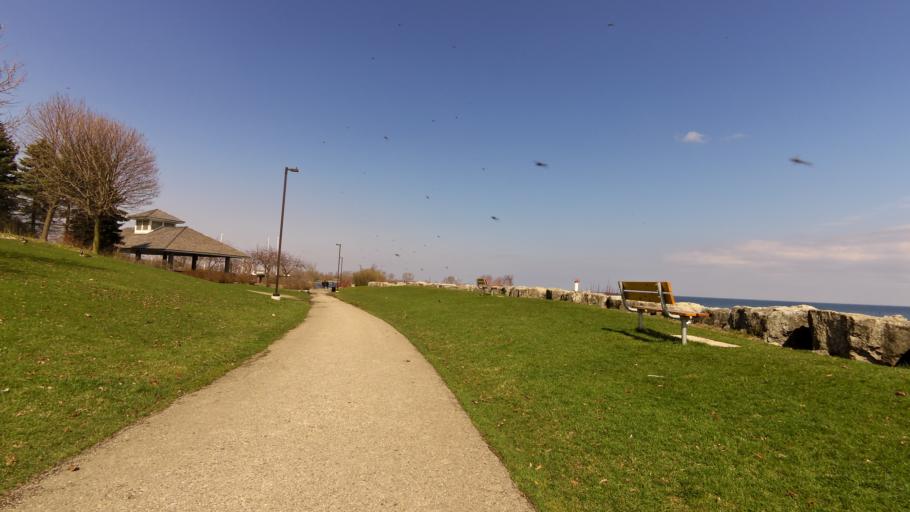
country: CA
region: Ontario
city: Etobicoke
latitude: 43.5626
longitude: -79.5577
